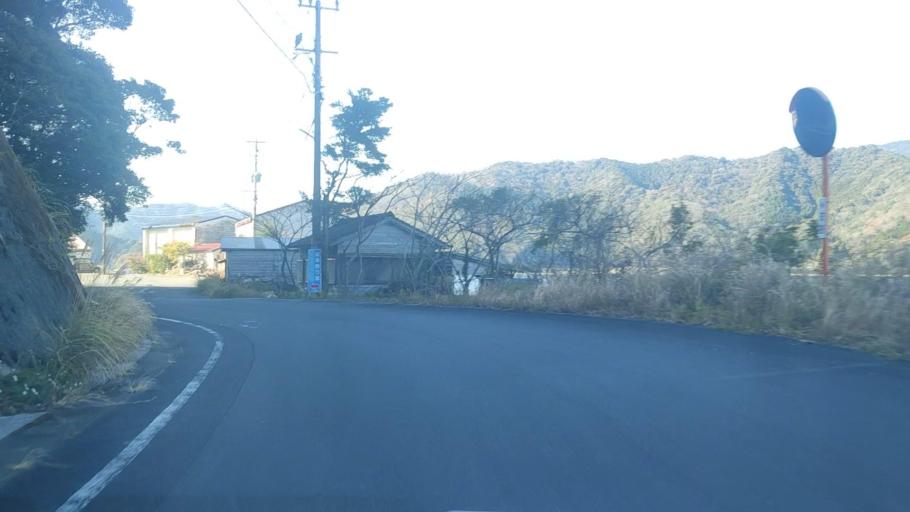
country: JP
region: Oita
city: Saiki
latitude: 32.7968
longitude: 131.8973
